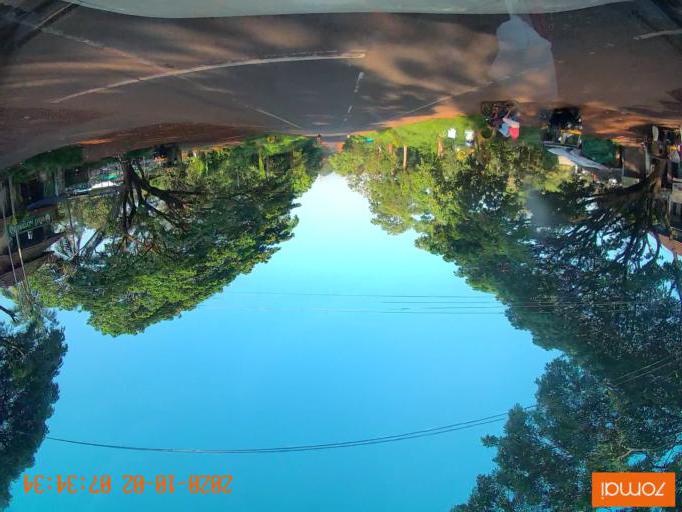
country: IN
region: Kerala
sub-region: Malappuram
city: Pariyapuram
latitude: 11.0638
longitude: 75.9285
